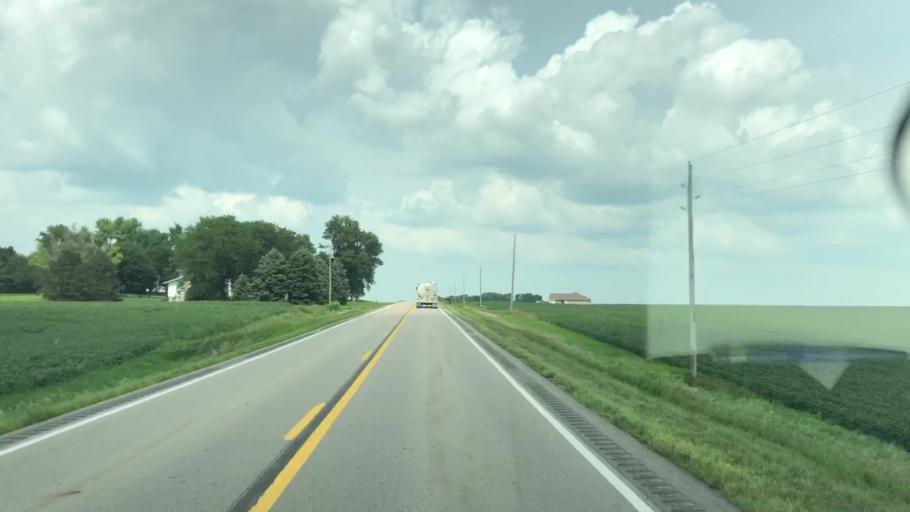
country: US
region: Iowa
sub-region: Plymouth County
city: Remsen
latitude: 42.7894
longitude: -95.9578
